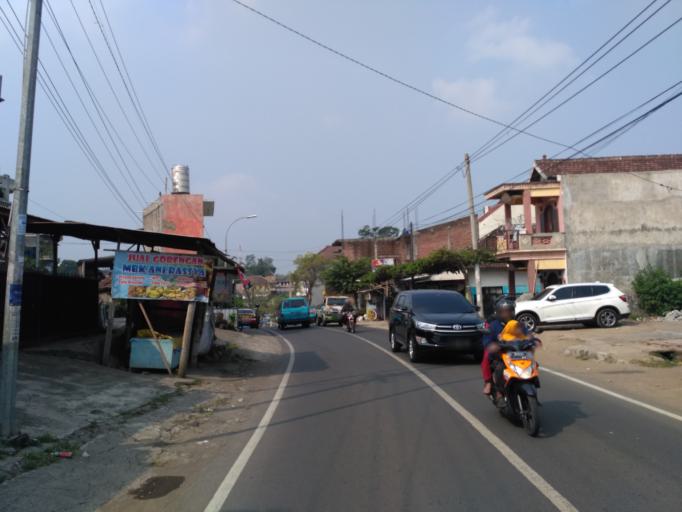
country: ID
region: East Java
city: Batu
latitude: -7.8641
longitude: 112.5526
